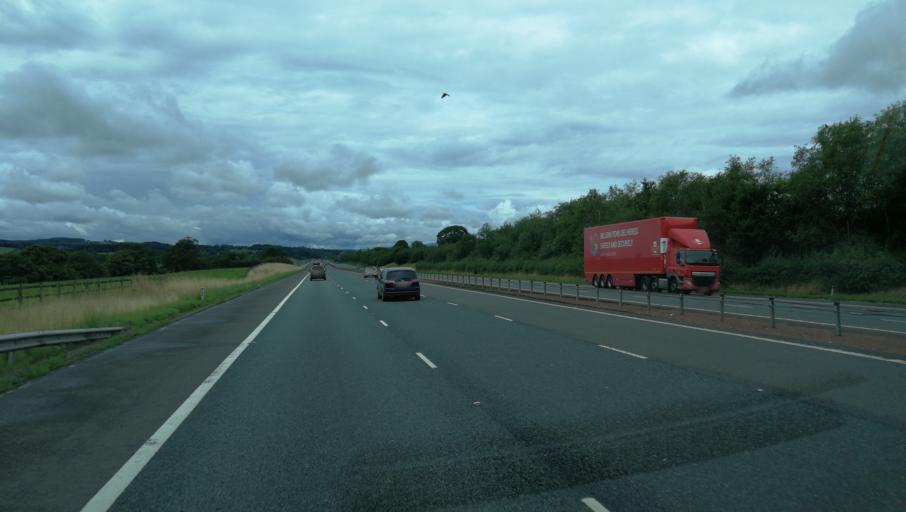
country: GB
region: Scotland
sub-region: Dumfries and Galloway
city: Lochmaben
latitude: 55.1852
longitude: -3.4068
